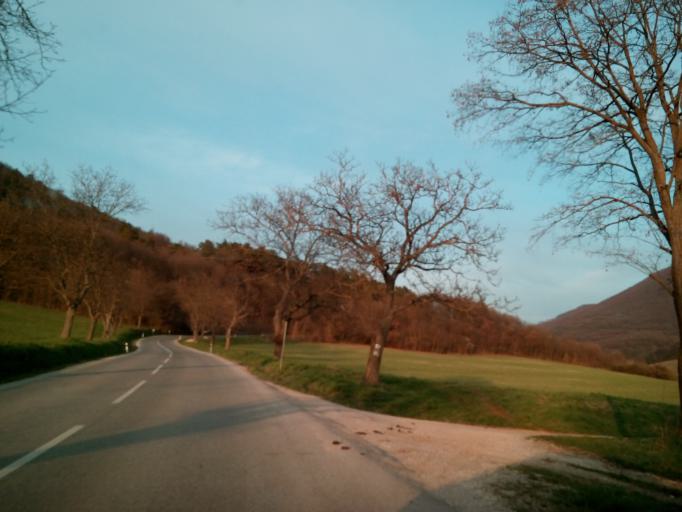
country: SK
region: Kosicky
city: Dobsina
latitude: 48.6622
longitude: 20.3762
